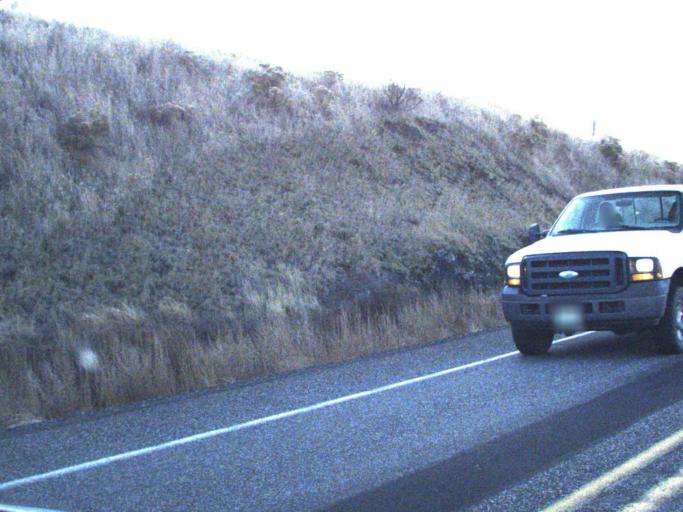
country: US
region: Washington
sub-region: Walla Walla County
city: Burbank
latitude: 46.0724
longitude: -118.7879
